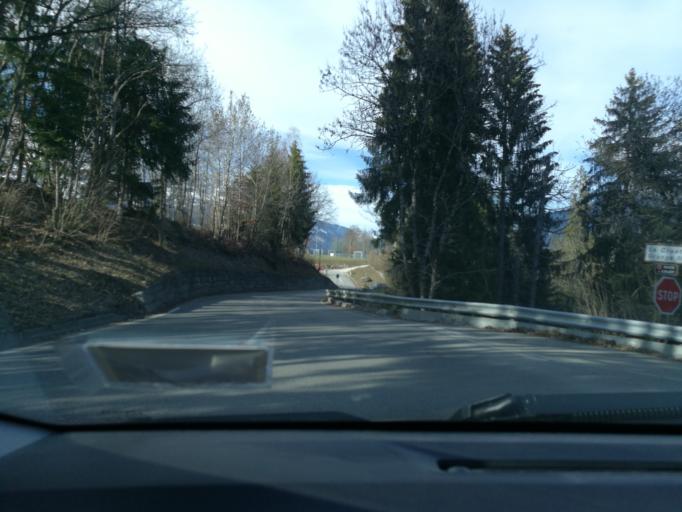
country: FR
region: Rhone-Alpes
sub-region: Departement de la Haute-Savoie
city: Combloux
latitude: 45.8971
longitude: 6.6514
